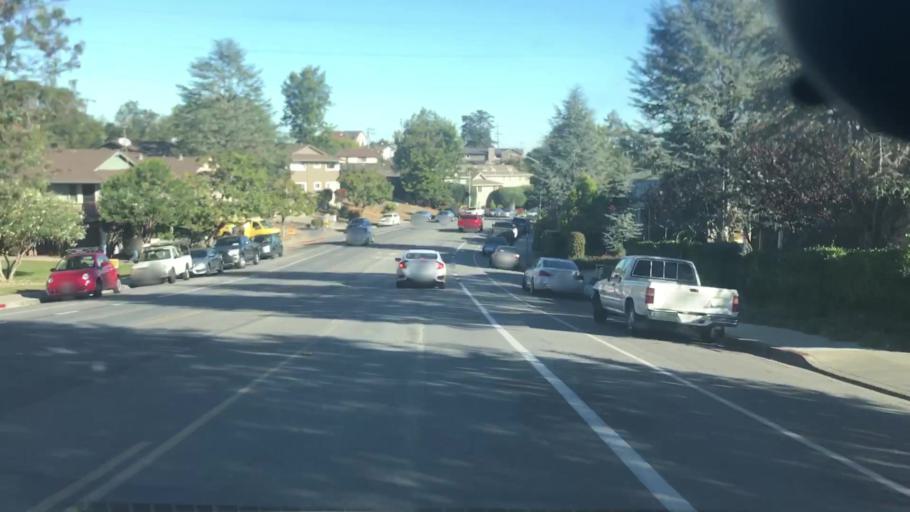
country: US
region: California
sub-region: San Mateo County
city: Emerald Lake Hills
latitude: 37.4634
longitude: -122.2498
